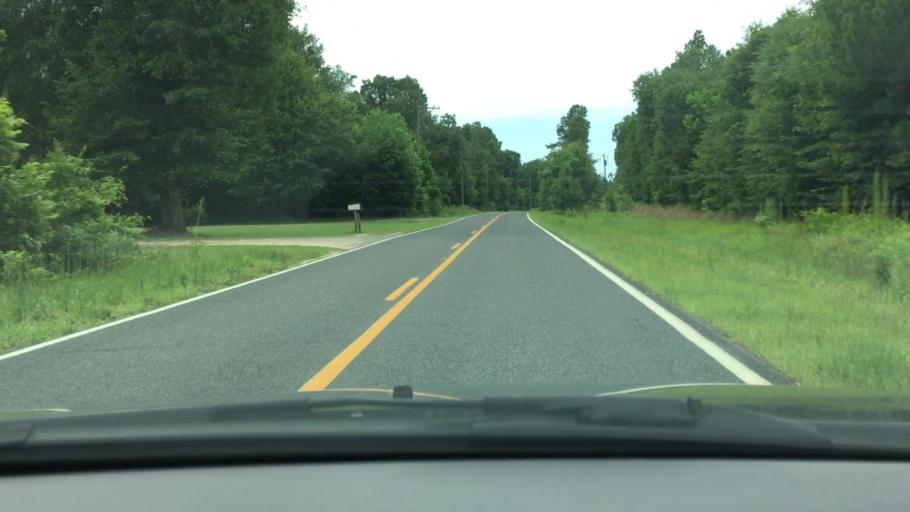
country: US
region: South Carolina
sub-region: Barnwell County
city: Williston
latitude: 33.6332
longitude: -81.3651
